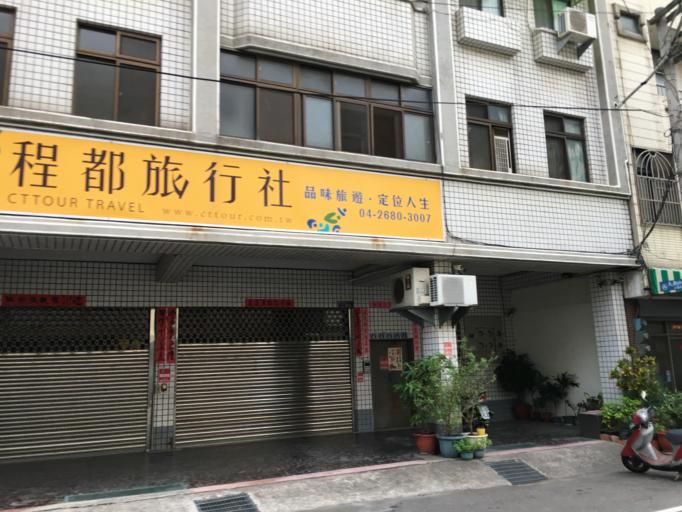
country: TW
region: Taiwan
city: Fengyuan
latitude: 24.3505
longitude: 120.6269
